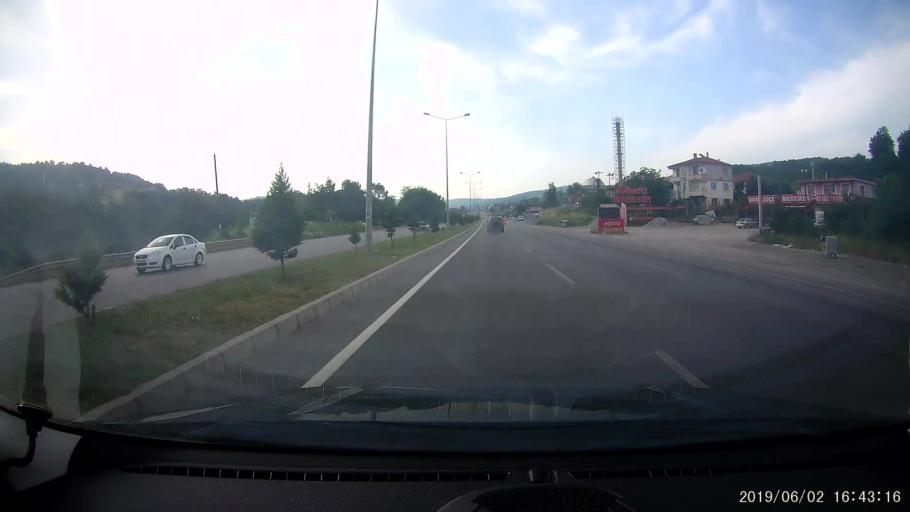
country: TR
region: Samsun
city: Kavak
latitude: 41.1324
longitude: 36.1307
